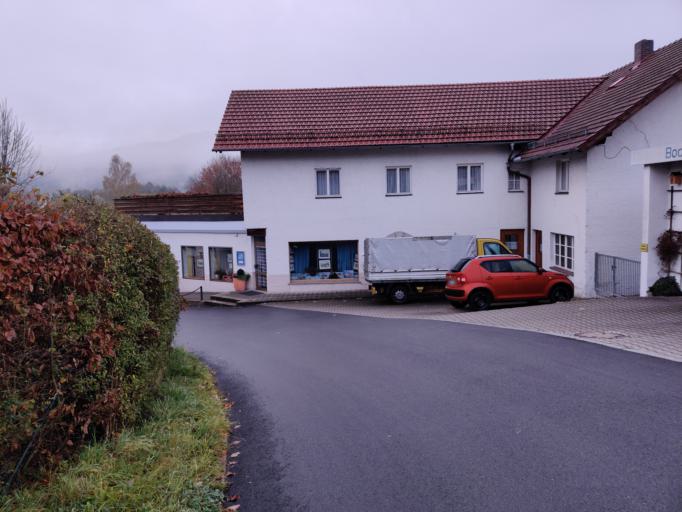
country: DE
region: Bavaria
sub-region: Upper Palatinate
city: Lam
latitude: 49.1939
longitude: 13.0534
